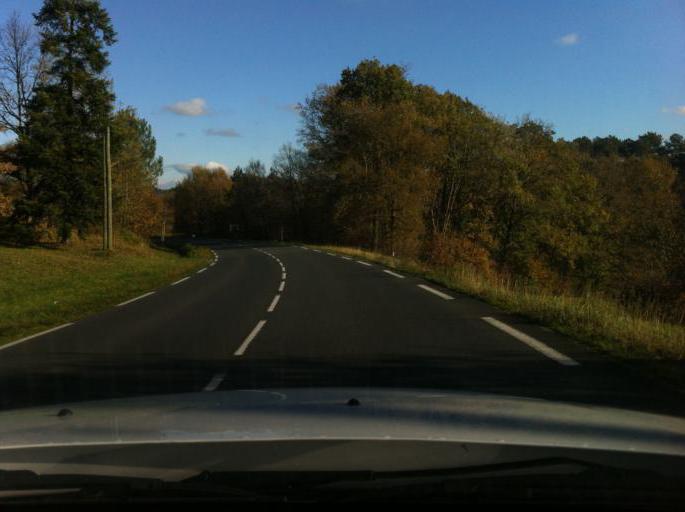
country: FR
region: Aquitaine
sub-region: Departement de la Dordogne
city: Rouffignac-Saint-Cernin-de-Reilhac
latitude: 45.0466
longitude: 0.8573
